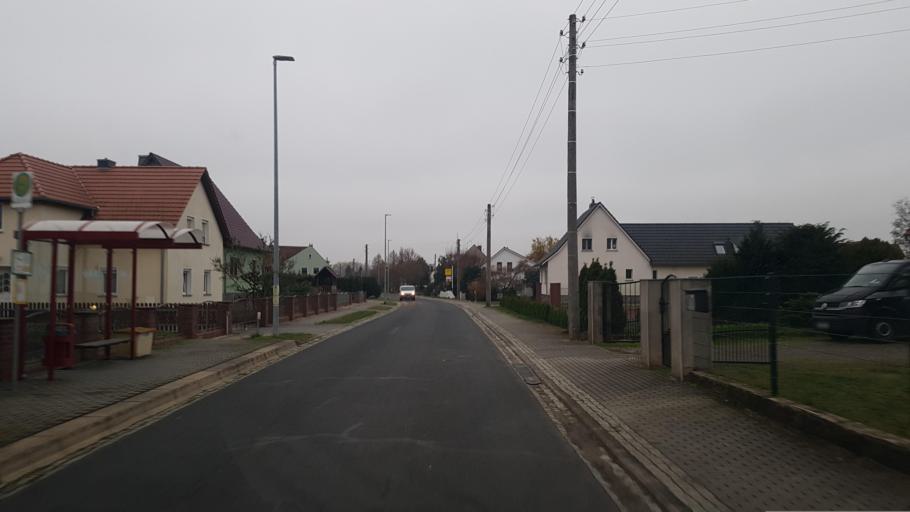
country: DE
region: Brandenburg
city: Hermsdorf
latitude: 51.4103
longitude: 13.8896
